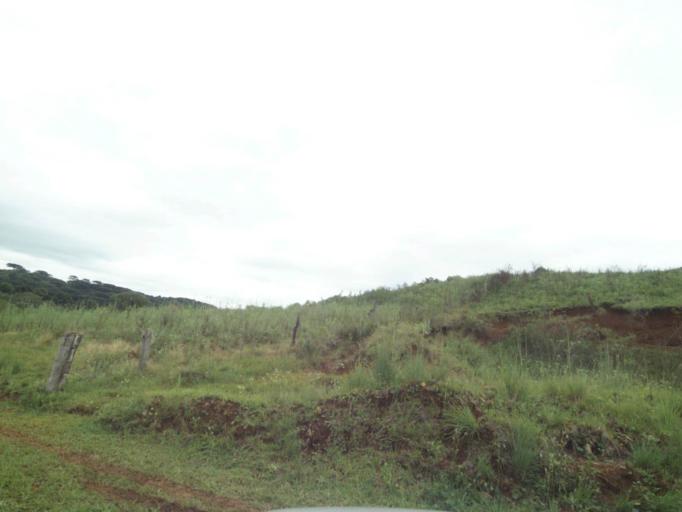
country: BR
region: Rio Grande do Sul
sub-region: Lagoa Vermelha
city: Lagoa Vermelha
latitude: -28.2256
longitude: -51.5421
